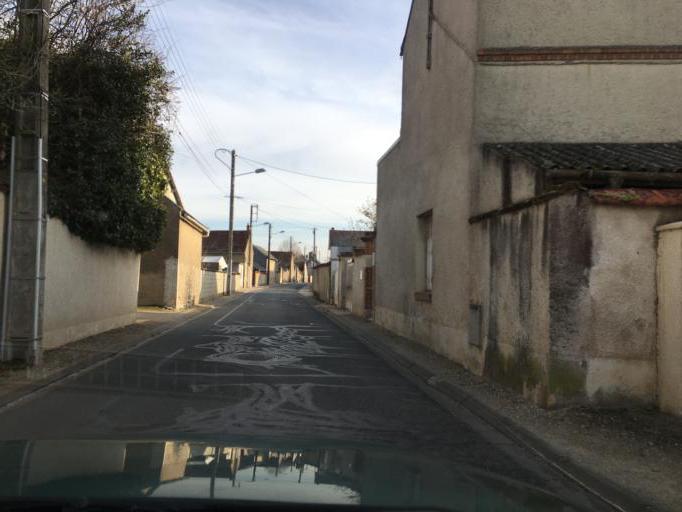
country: FR
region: Centre
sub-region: Departement du Loiret
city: Saint-Jean-le-Blanc
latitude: 47.8861
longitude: 1.9195
